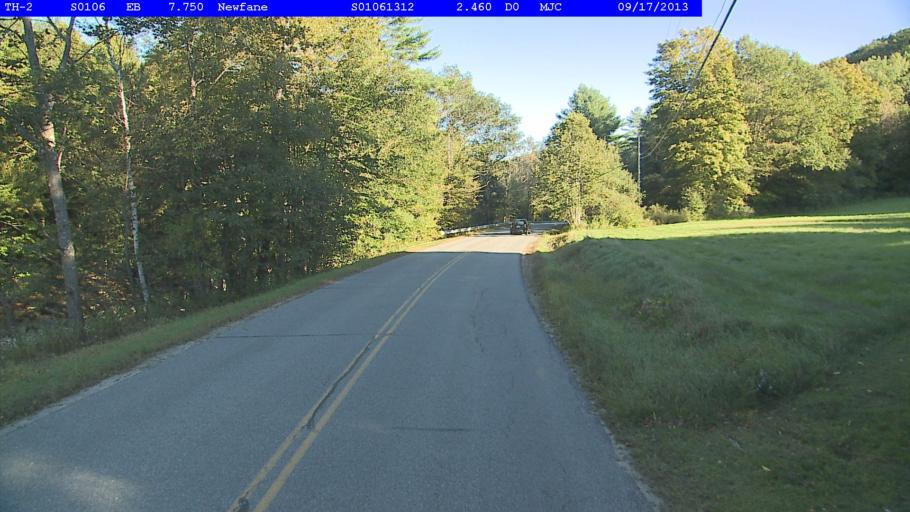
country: US
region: Vermont
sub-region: Windham County
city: Dover
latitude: 42.9421
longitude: -72.7240
